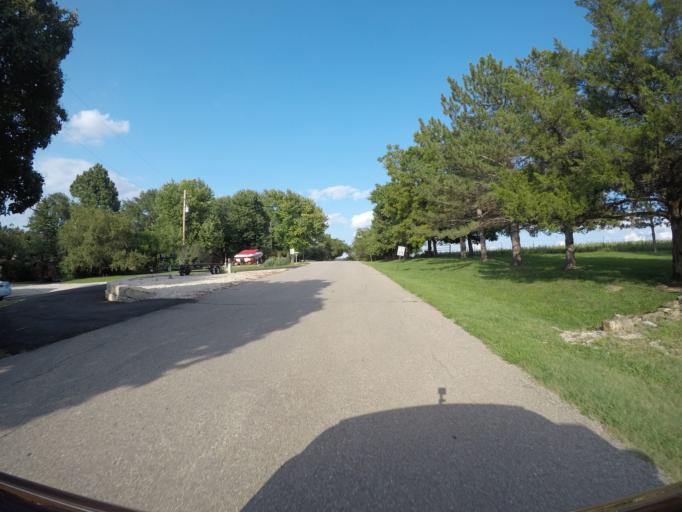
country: US
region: Kansas
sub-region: Wabaunsee County
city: Alma
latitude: 38.8611
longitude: -96.1827
